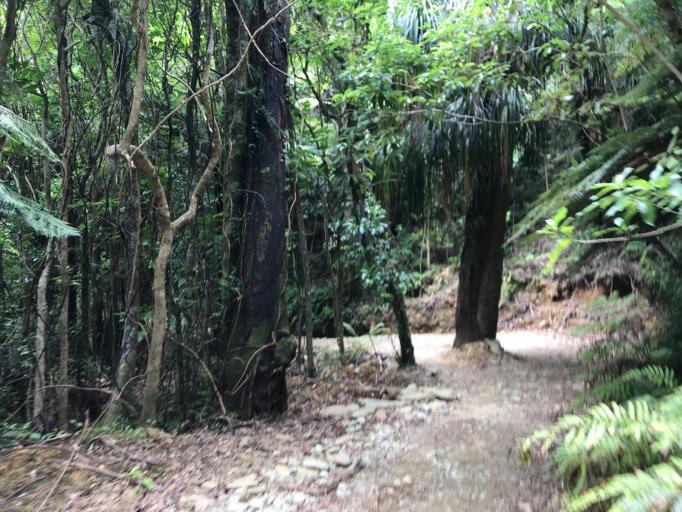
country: NZ
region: Marlborough
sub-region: Marlborough District
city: Picton
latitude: -41.0955
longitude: 174.1884
